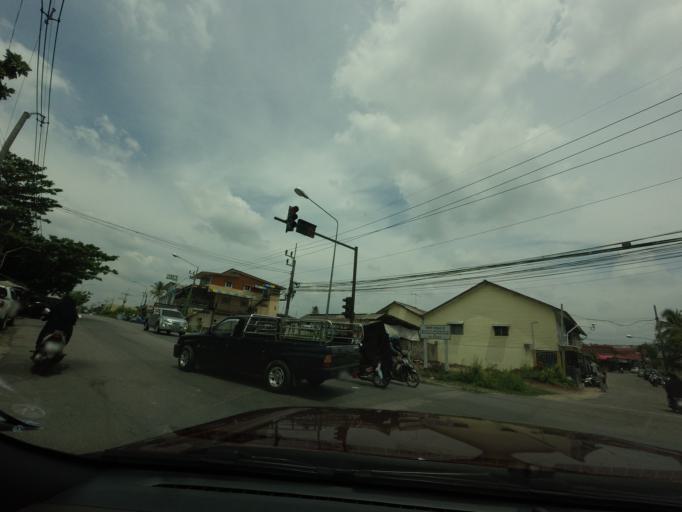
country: TH
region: Yala
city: Yala
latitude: 6.5592
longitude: 101.2972
